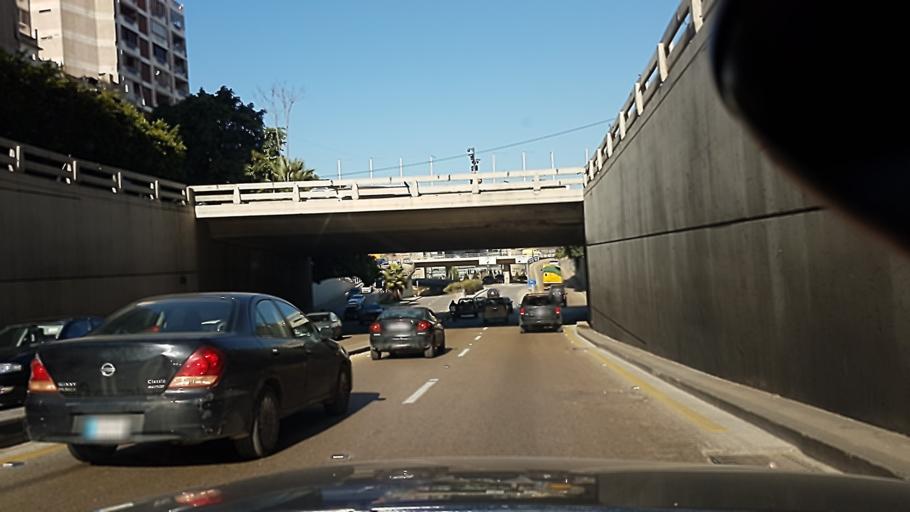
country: LB
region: Beyrouth
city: Beirut
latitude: 33.8917
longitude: 35.5008
